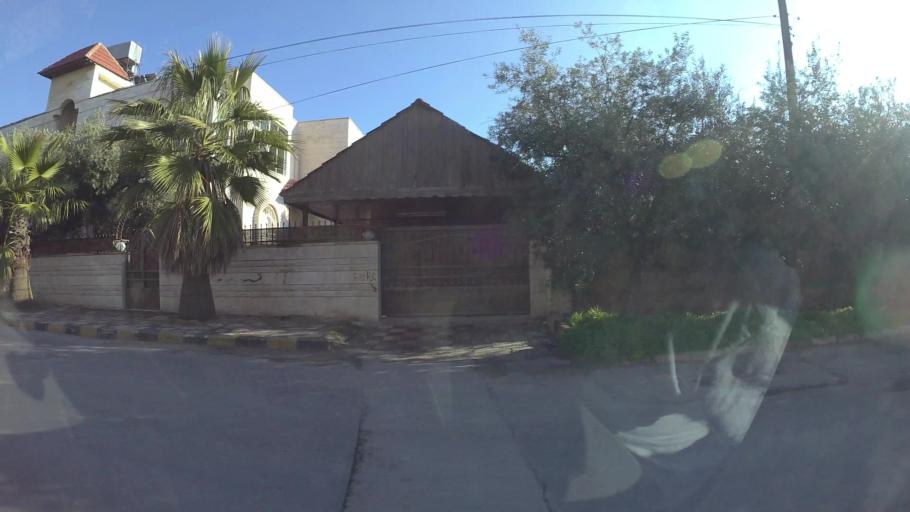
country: JO
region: Amman
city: Al Bunayyat ash Shamaliyah
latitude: 31.9007
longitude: 35.9180
